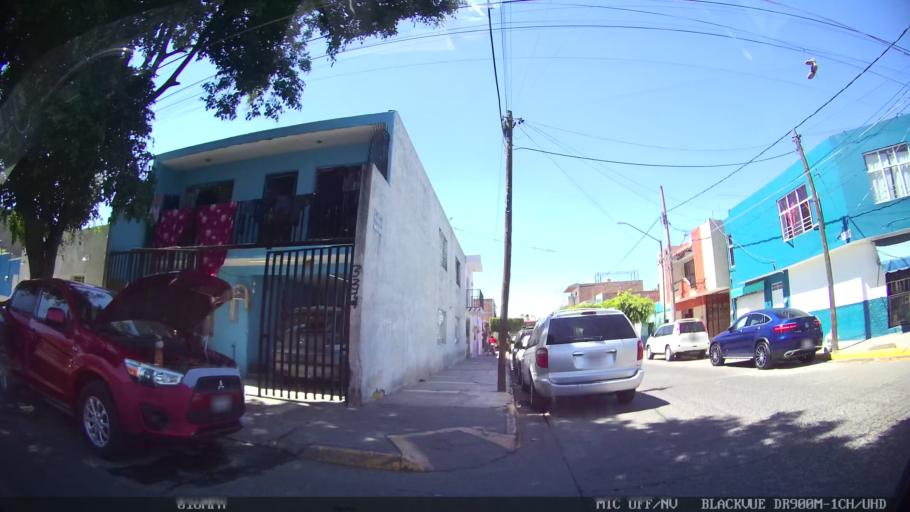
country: MX
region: Jalisco
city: Tlaquepaque
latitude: 20.6671
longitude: -103.2907
